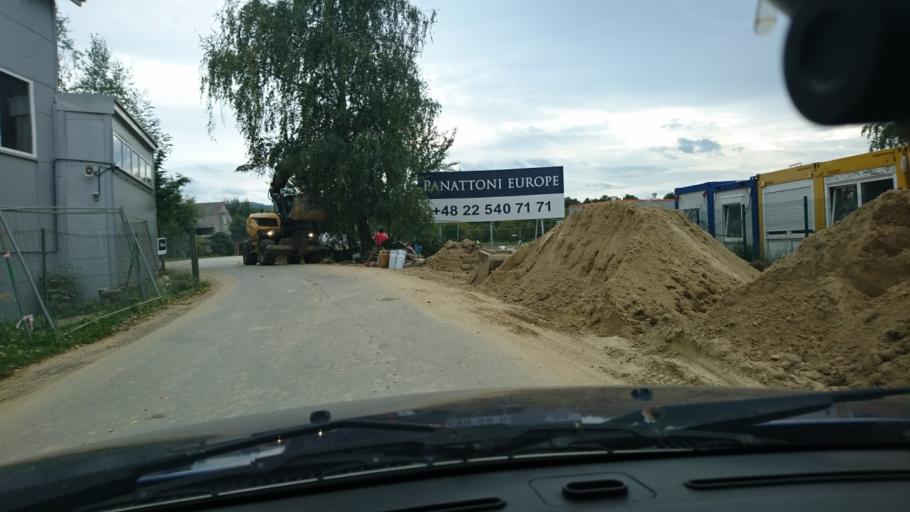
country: PL
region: Silesian Voivodeship
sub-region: Powiat bielski
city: Jaworze
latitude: 49.8211
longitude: 18.9676
